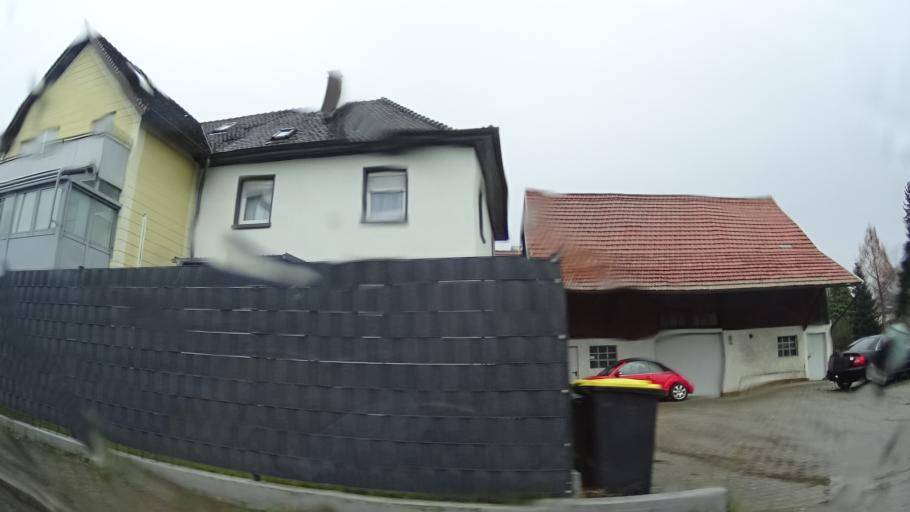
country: DE
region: Baden-Wuerttemberg
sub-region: Karlsruhe Region
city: Sinzheim
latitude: 48.7619
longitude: 8.1688
